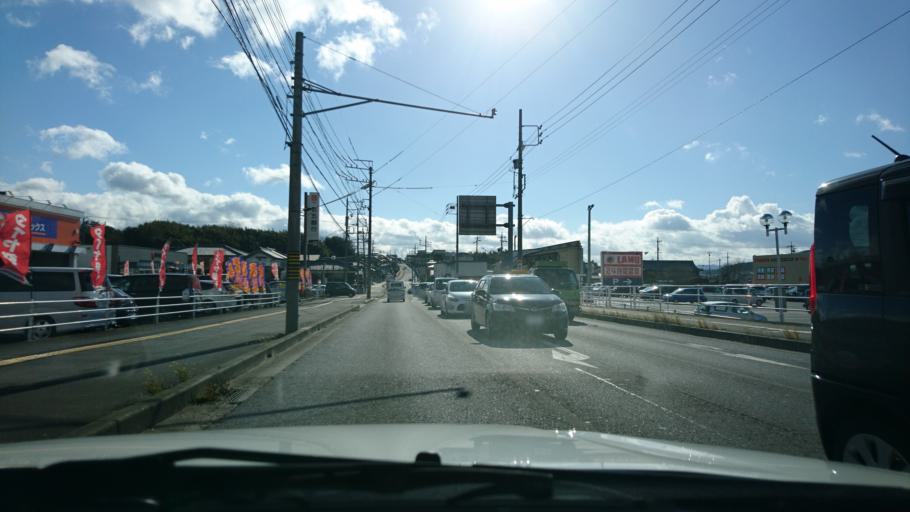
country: JP
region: Mie
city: Ueno-ebisumachi
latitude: 34.7751
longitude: 136.1238
